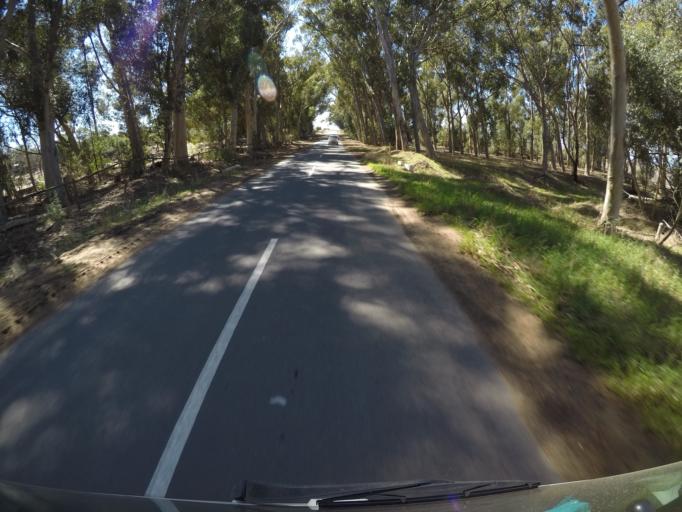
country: ZA
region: Western Cape
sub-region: City of Cape Town
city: Sunset Beach
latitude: -33.7492
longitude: 18.5576
